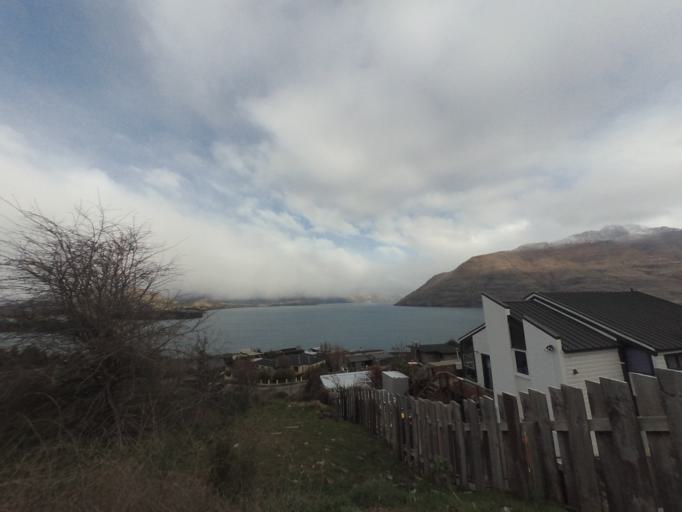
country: NZ
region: Otago
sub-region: Queenstown-Lakes District
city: Queenstown
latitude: -45.0402
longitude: 168.6336
